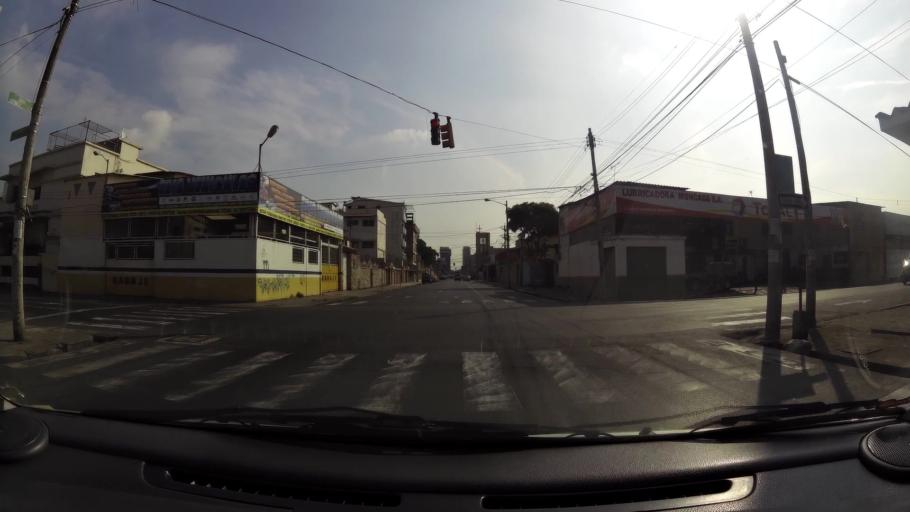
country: EC
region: Guayas
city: Guayaquil
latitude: -2.1925
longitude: -79.8971
